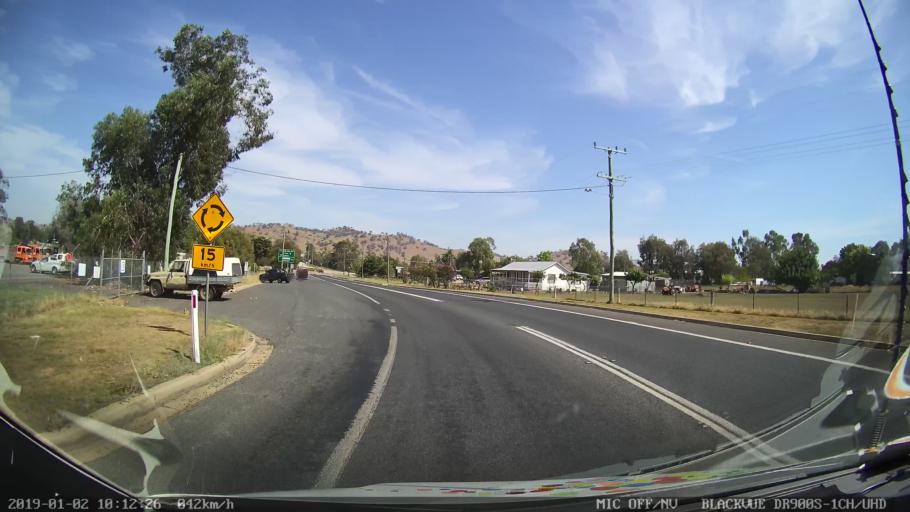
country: AU
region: New South Wales
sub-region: Gundagai
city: Gundagai
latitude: -35.0850
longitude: 148.0952
